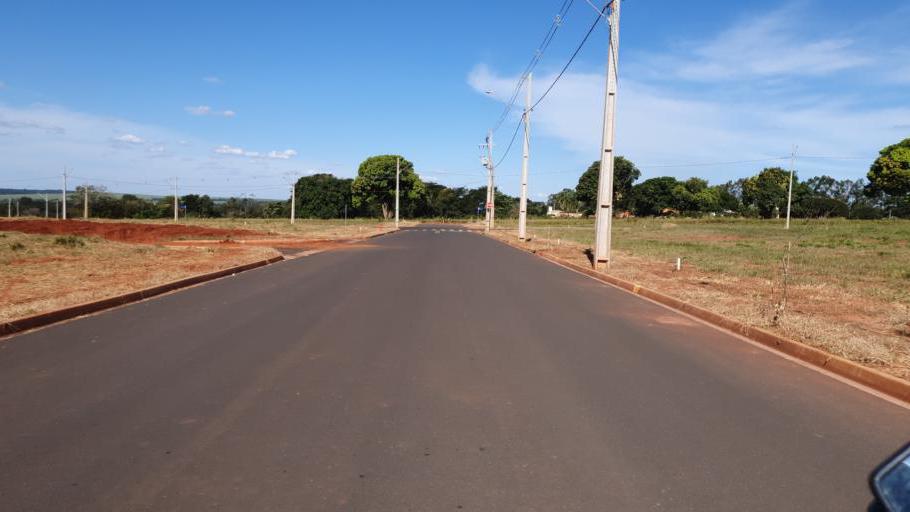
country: BR
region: Sao Paulo
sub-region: Paraguacu Paulista
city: Paraguacu Paulista
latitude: -22.3984
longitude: -50.5761
